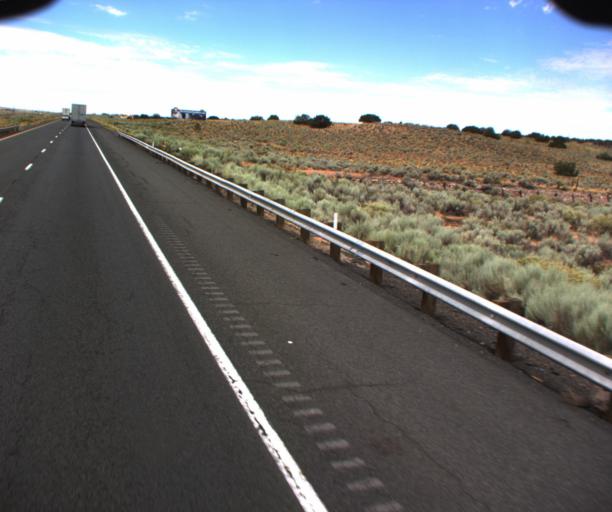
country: US
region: Arizona
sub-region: Apache County
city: Houck
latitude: 35.1514
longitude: -109.5066
